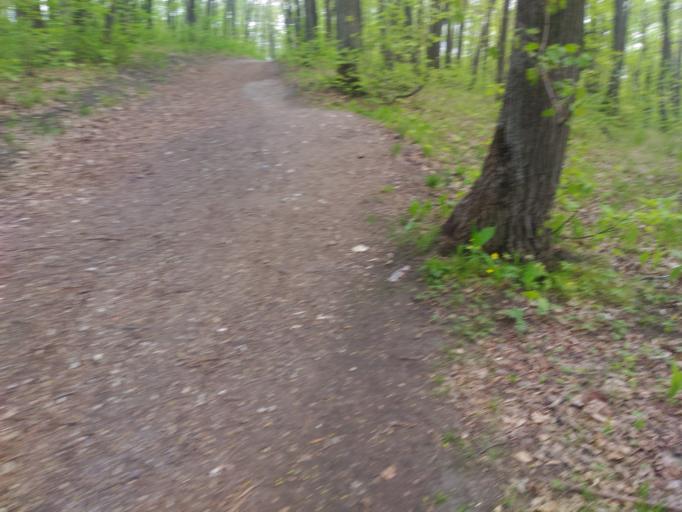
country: RU
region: Ulyanovsk
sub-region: Ulyanovskiy Rayon
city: Ulyanovsk
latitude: 54.2722
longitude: 48.3414
